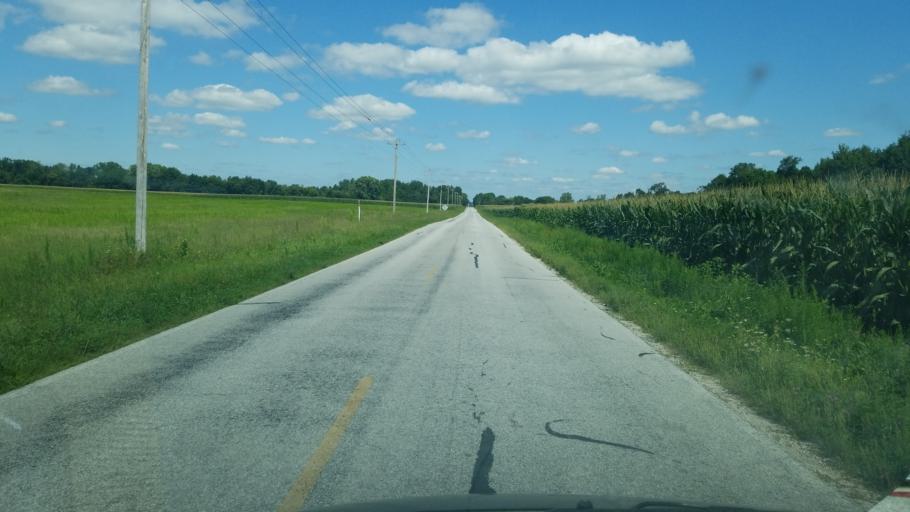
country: US
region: Ohio
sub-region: Fulton County
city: Swanton
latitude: 41.5308
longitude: -83.9409
